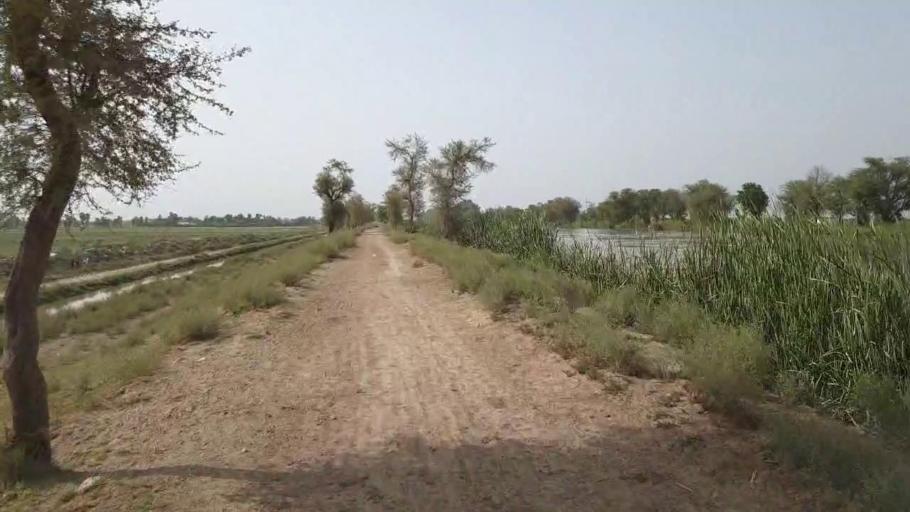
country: PK
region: Sindh
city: Daur
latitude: 26.4456
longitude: 68.1605
